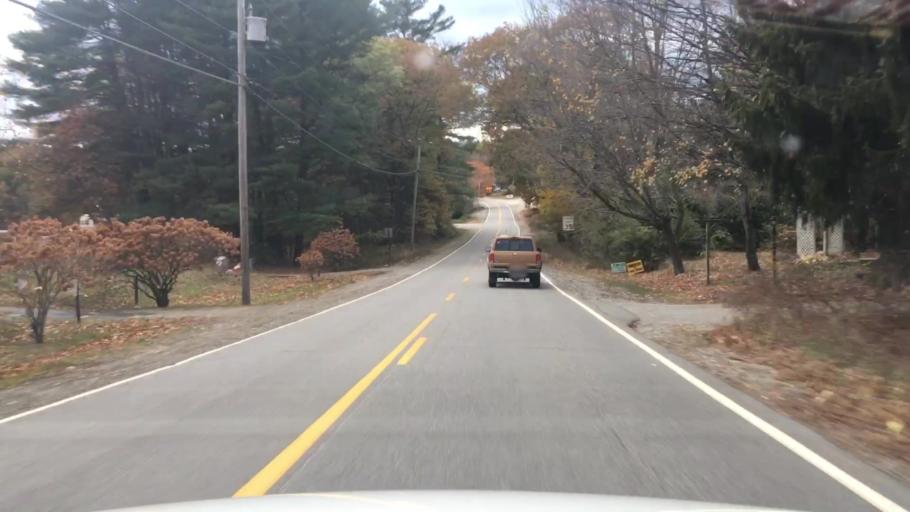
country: US
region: Maine
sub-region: Androscoggin County
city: Livermore
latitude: 44.3397
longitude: -70.2445
